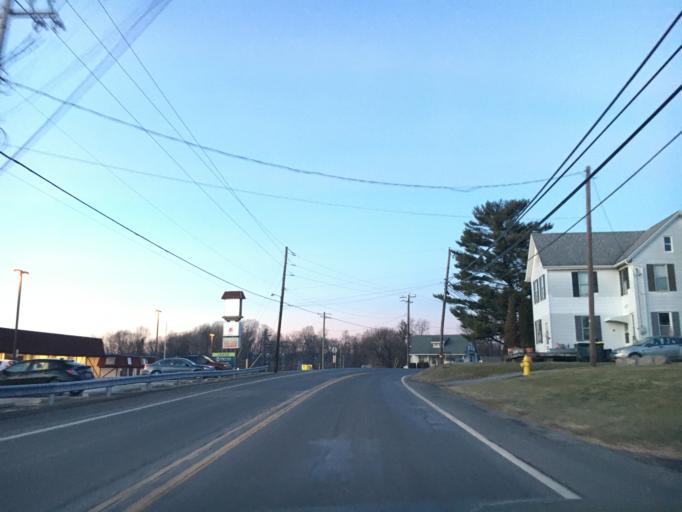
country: US
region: Pennsylvania
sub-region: Lehigh County
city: Schnecksville
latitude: 40.6838
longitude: -75.6133
